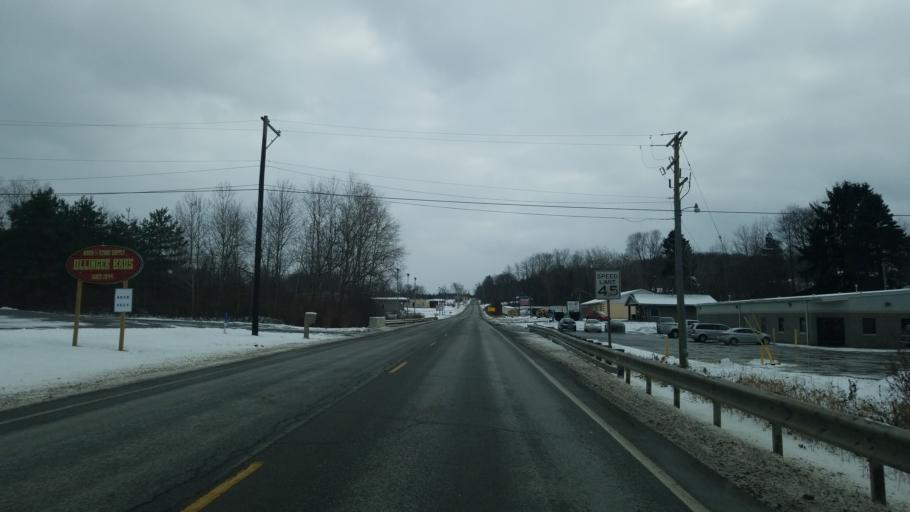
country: US
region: Pennsylvania
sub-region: Clearfield County
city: Sandy
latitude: 41.0876
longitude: -78.7669
